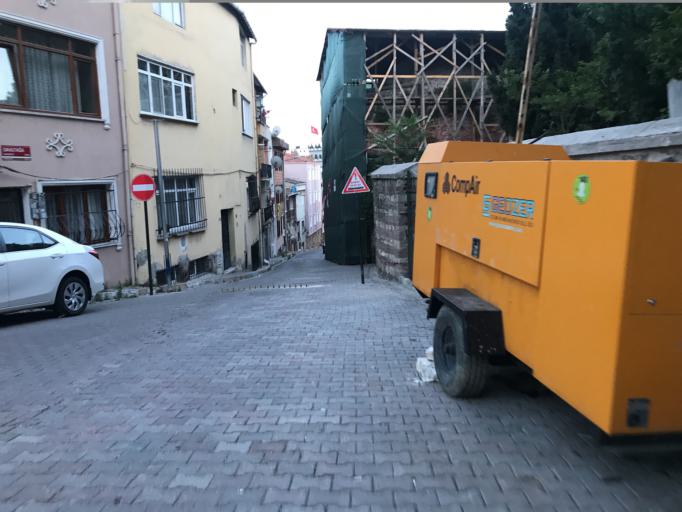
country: TR
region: Istanbul
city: Istanbul
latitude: 41.0404
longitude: 28.9309
